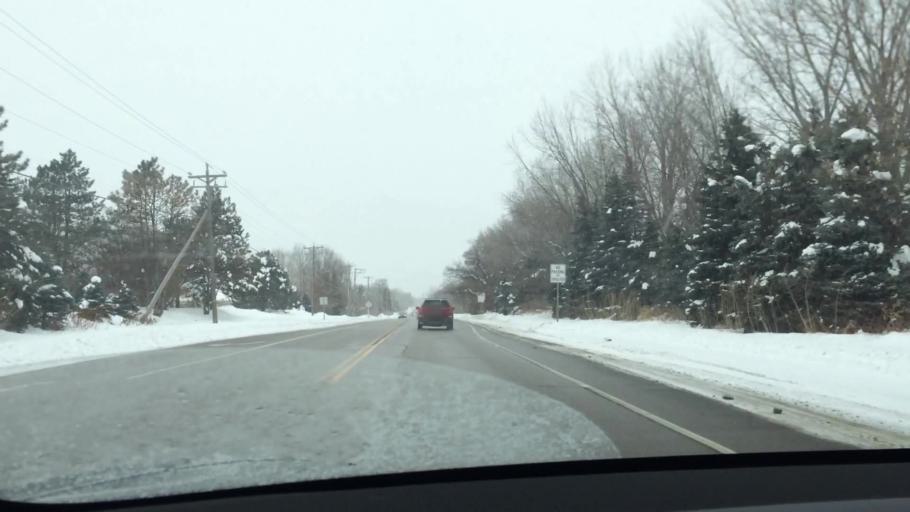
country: US
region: Minnesota
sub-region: Ramsey County
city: Shoreview
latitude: 45.1101
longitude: -93.1273
